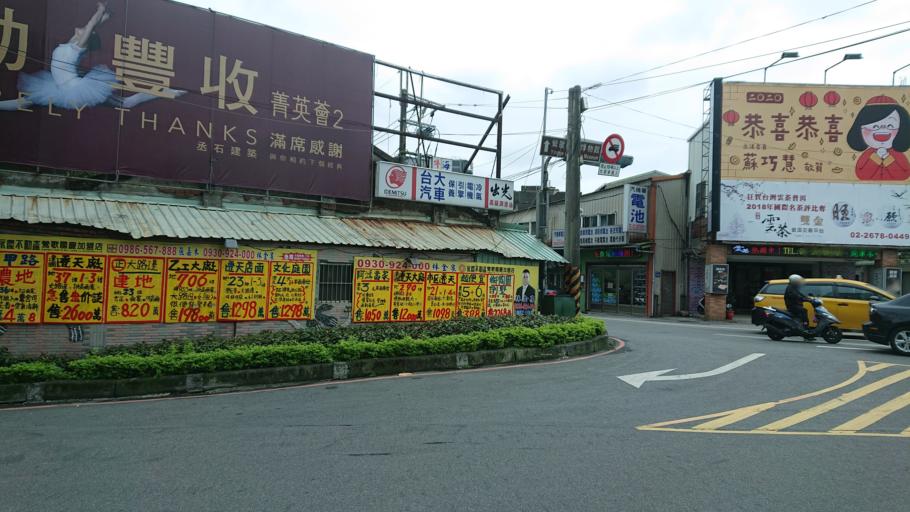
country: TW
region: Taiwan
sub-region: Taoyuan
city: Taoyuan
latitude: 24.9568
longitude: 121.3535
